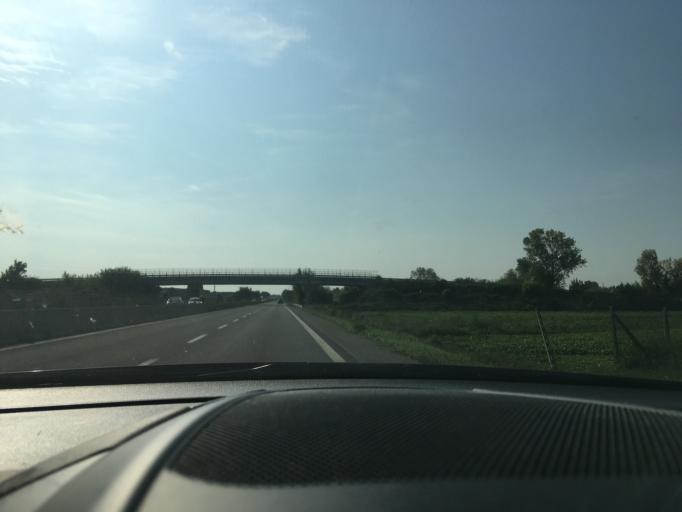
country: IT
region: Emilia-Romagna
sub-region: Provincia di Rimini
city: Bellaria-Igea Marina
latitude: 44.1342
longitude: 12.4638
